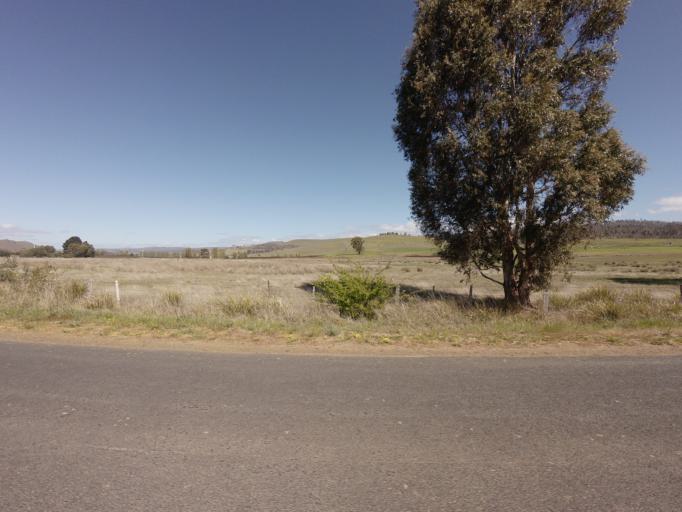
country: AU
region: Tasmania
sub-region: Derwent Valley
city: New Norfolk
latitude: -42.5367
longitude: 146.7289
